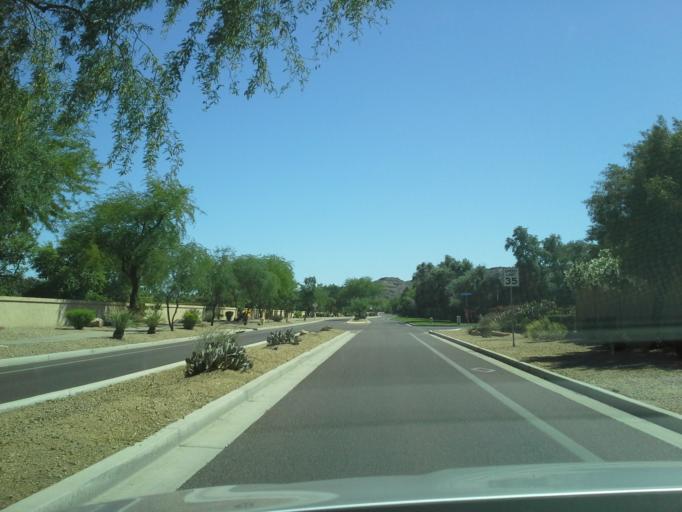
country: US
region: Arizona
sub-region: Maricopa County
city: Paradise Valley
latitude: 33.5591
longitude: -111.9435
